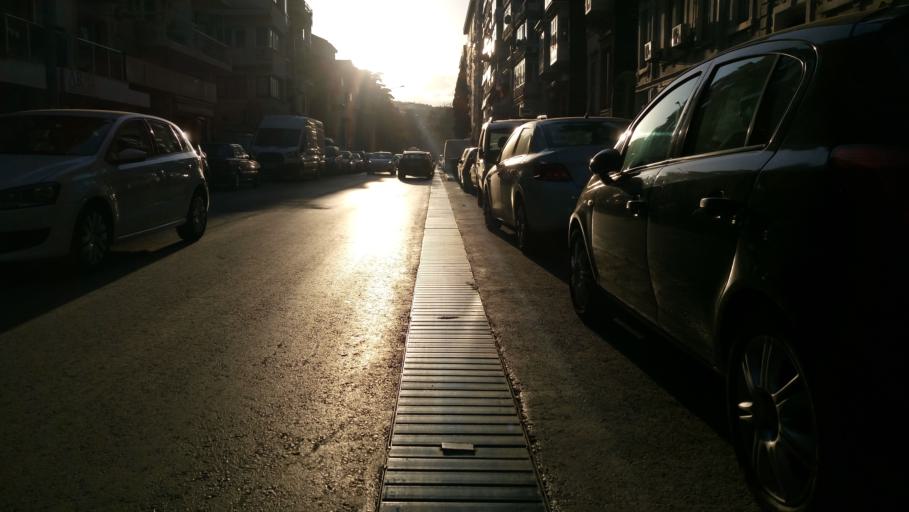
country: TR
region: Izmir
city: Izmir
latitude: 38.4087
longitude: 27.1104
